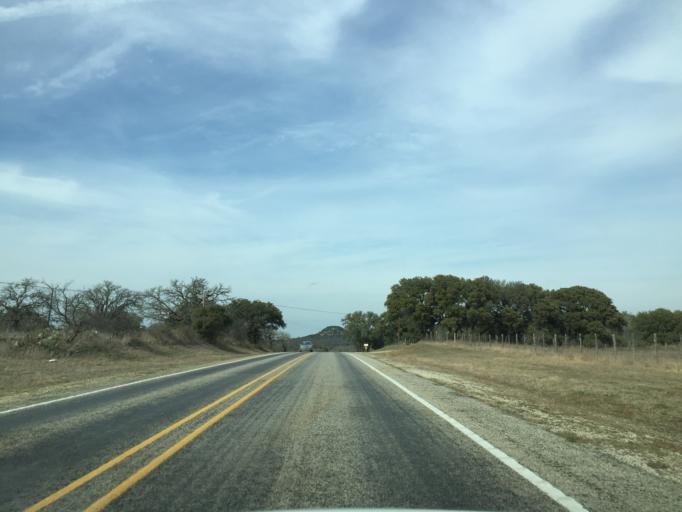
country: US
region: Texas
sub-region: Gillespie County
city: Fredericksburg
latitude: 30.4345
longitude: -98.7372
